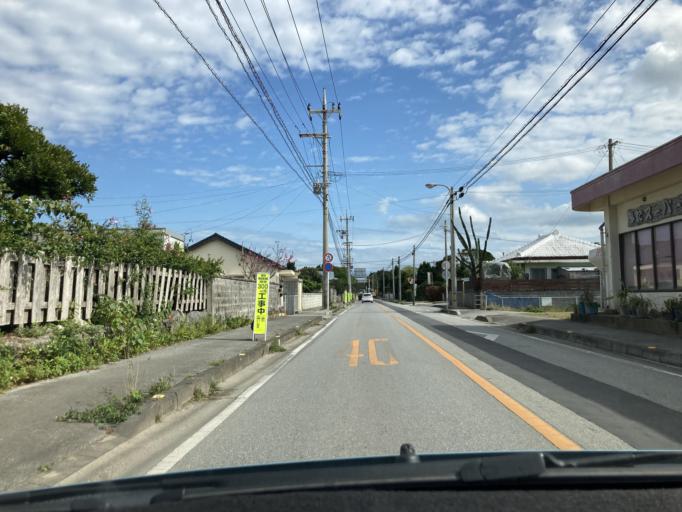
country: JP
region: Okinawa
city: Nago
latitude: 26.7010
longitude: 127.9270
